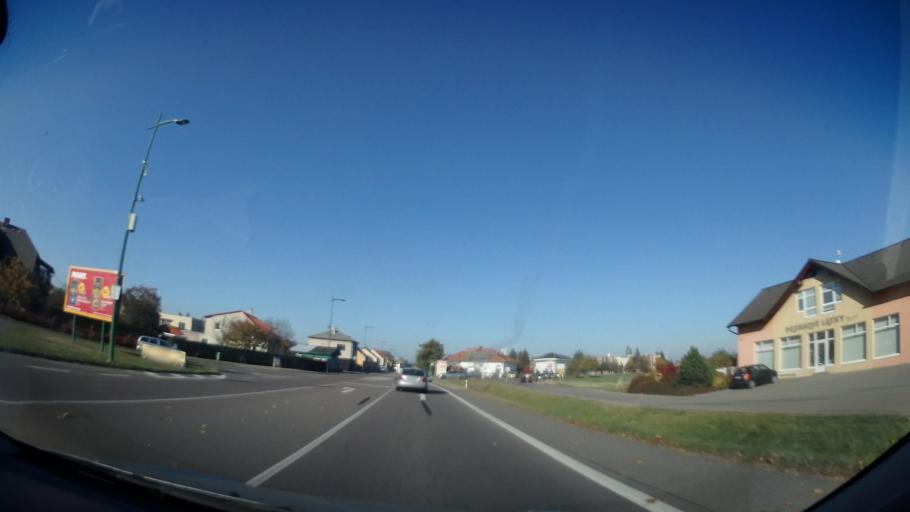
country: CZ
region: Pardubicky
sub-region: Okres Chrudim
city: Slatinany
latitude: 49.9112
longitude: 15.8187
